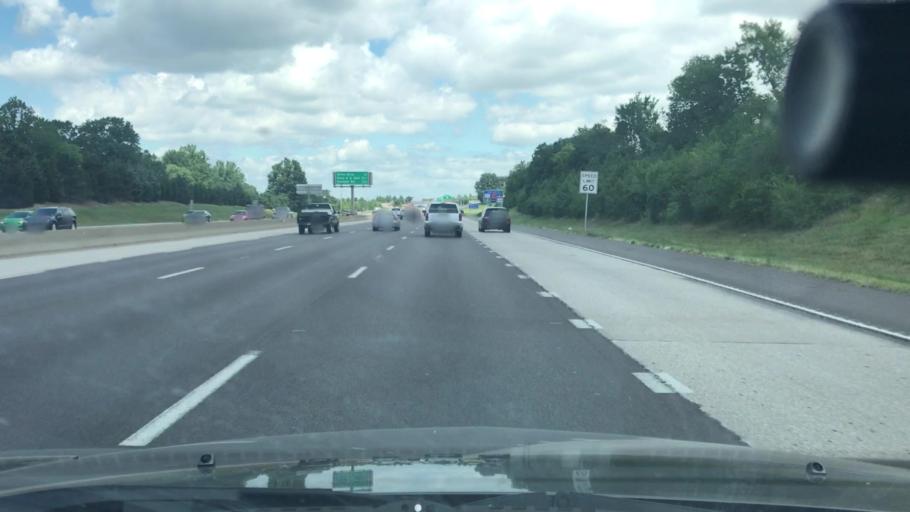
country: US
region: Missouri
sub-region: Saint Louis County
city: Creve Coeur
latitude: 38.6623
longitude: -90.4484
